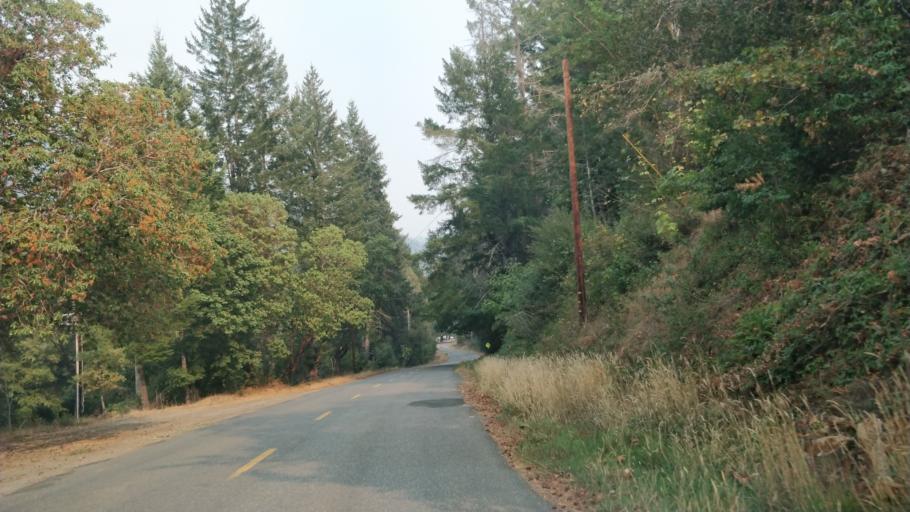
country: US
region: California
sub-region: Humboldt County
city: Rio Dell
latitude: 40.2430
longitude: -124.1277
